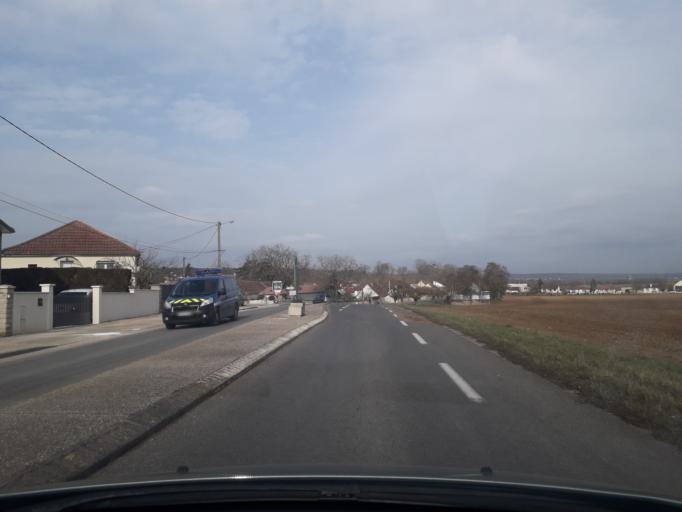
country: FR
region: Bourgogne
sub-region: Departement de la Cote-d'Or
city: Ahuy
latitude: 47.3663
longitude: 5.0268
